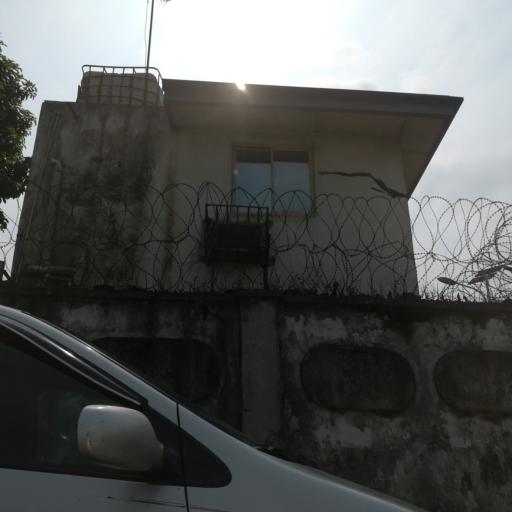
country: NG
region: Rivers
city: Port Harcourt
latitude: 4.8365
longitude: 7.0678
